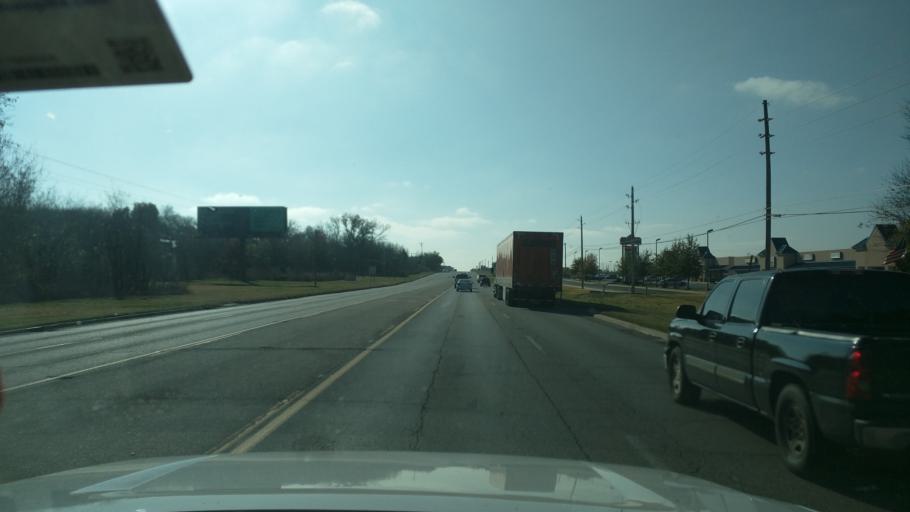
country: US
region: Oklahoma
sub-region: Washington County
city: Bartlesville
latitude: 36.7066
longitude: -95.9352
